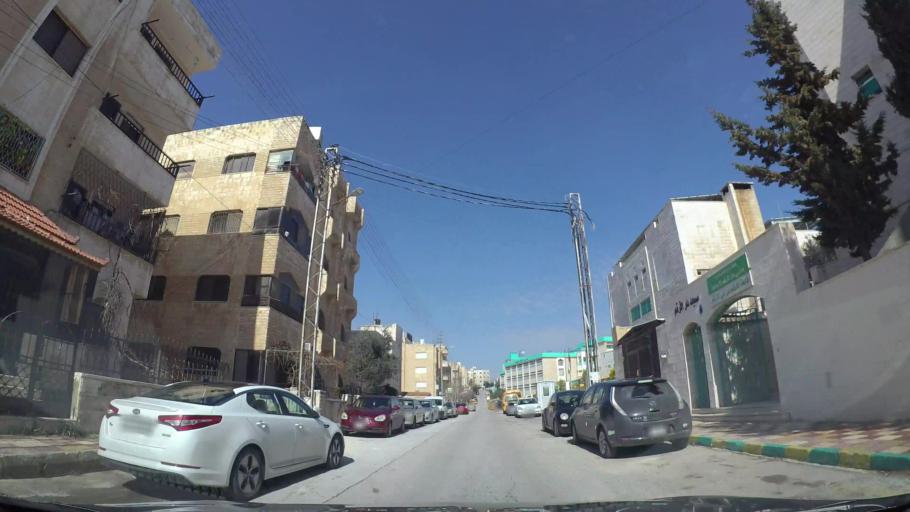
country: JO
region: Amman
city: Al Jubayhah
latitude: 31.9981
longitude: 35.8949
